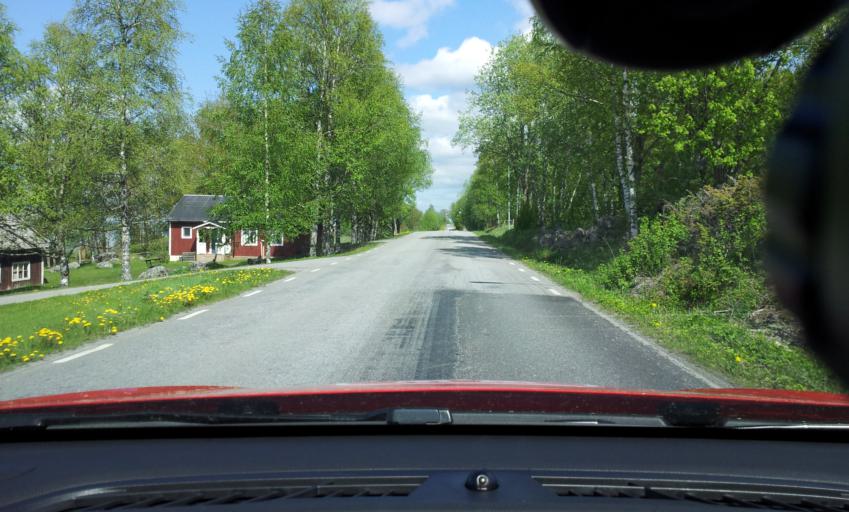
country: SE
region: Jaemtland
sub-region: Bergs Kommun
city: Hoverberg
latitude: 62.9521
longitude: 14.4909
